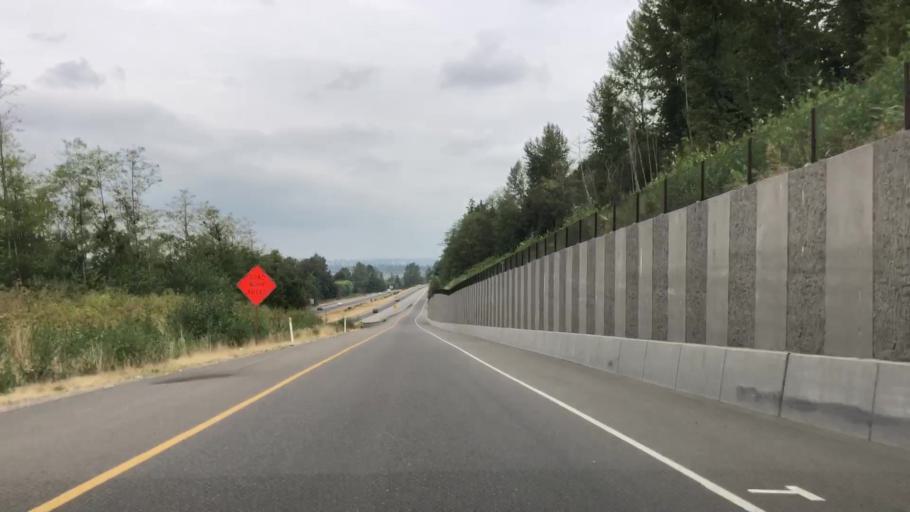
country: US
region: Washington
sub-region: Snohomish County
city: Fobes Hill
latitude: 47.9613
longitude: -122.1220
